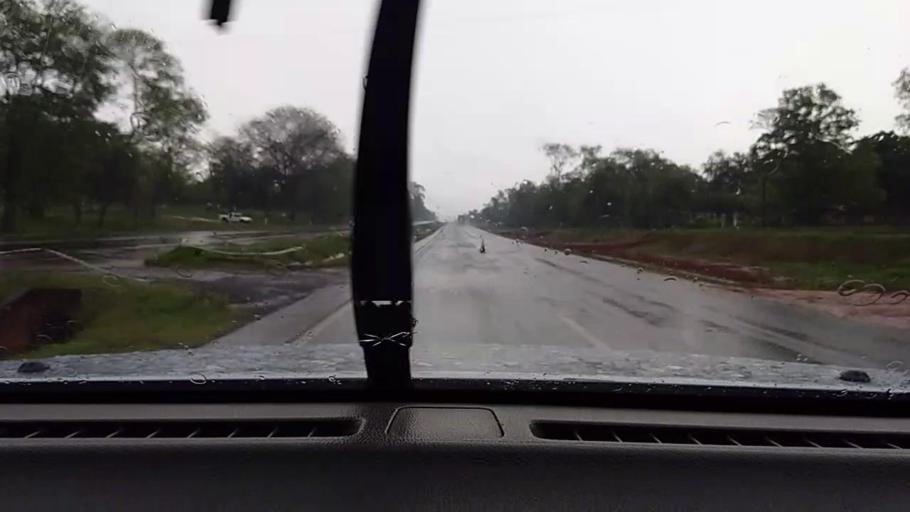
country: PY
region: Caaguazu
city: Repatriacion
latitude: -25.4491
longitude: -55.8966
